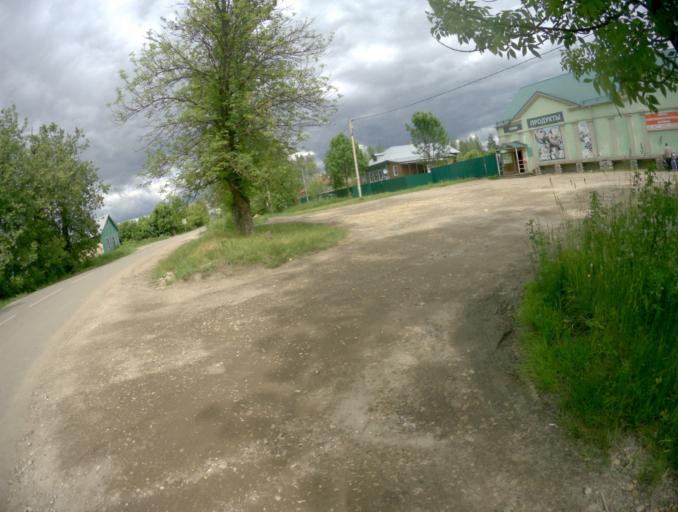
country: RU
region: Ivanovo
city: Savino
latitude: 56.5891
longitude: 41.2134
